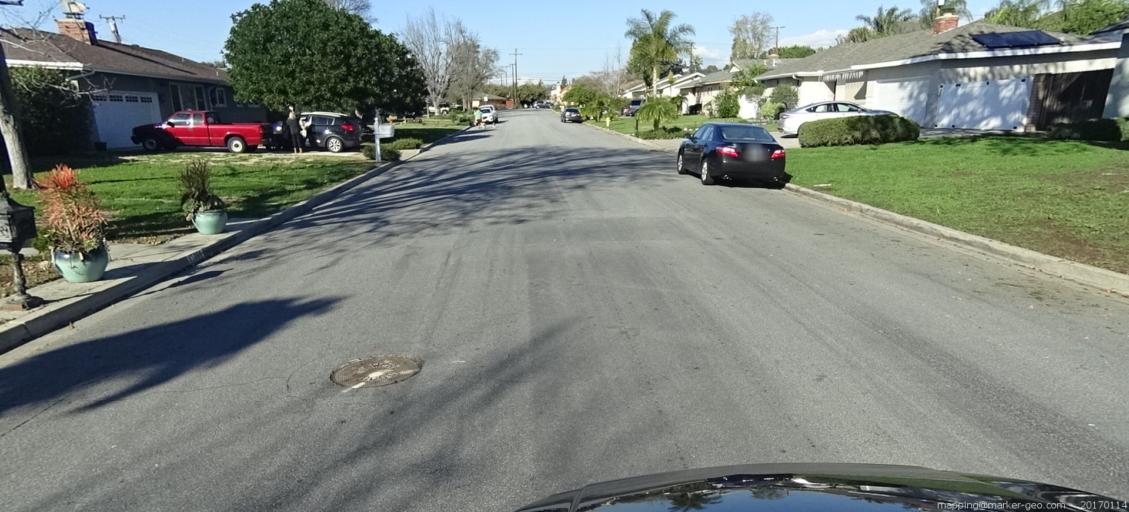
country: US
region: California
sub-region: Orange County
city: North Tustin
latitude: 33.7717
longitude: -117.8146
